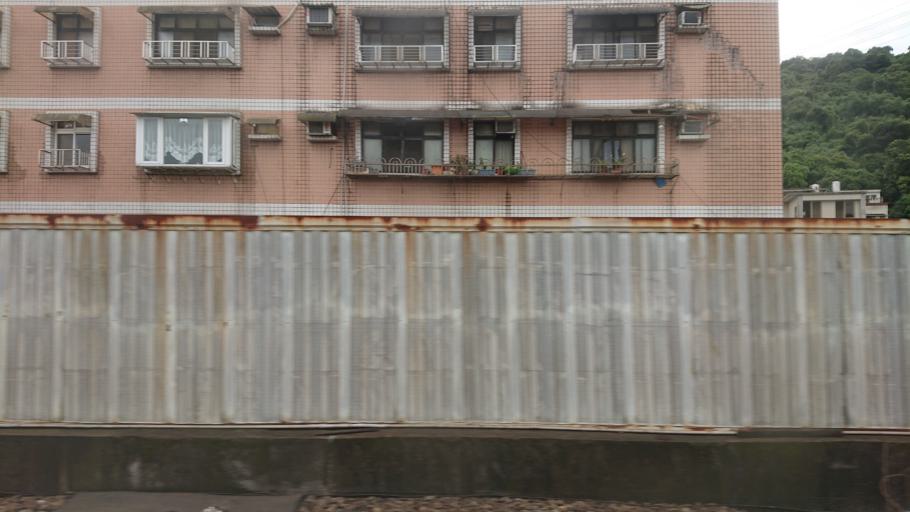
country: TW
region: Taiwan
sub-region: Keelung
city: Keelung
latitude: 25.1017
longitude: 121.7248
